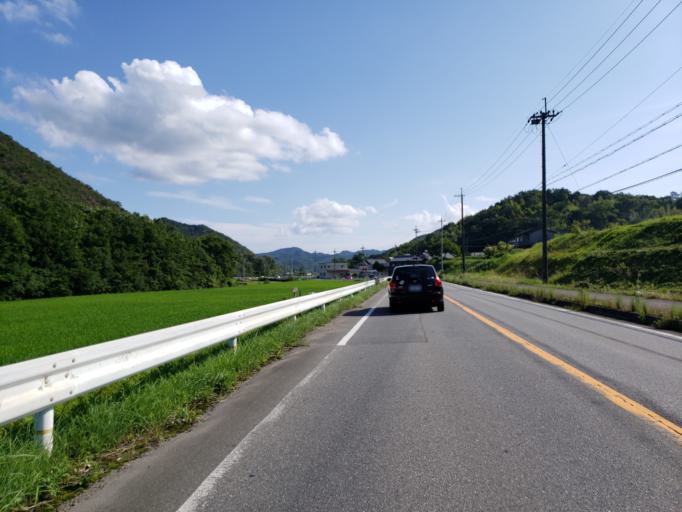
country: JP
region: Hyogo
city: Kakogawacho-honmachi
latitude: 34.8826
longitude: 134.8005
